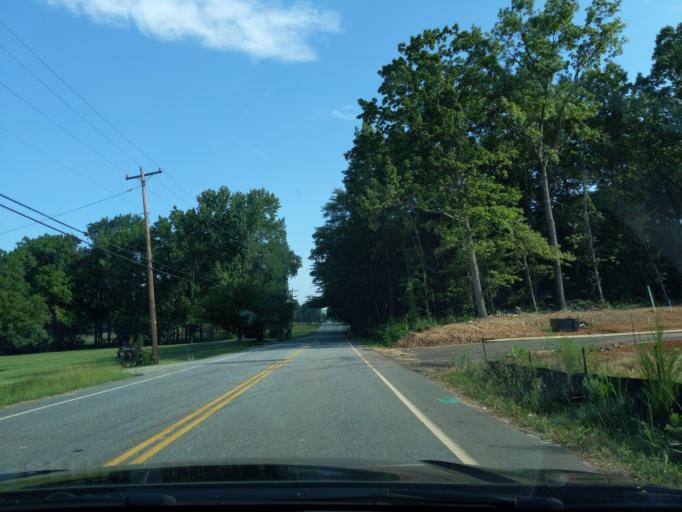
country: US
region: South Carolina
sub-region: Greenville County
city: Mauldin
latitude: 34.8123
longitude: -82.3112
